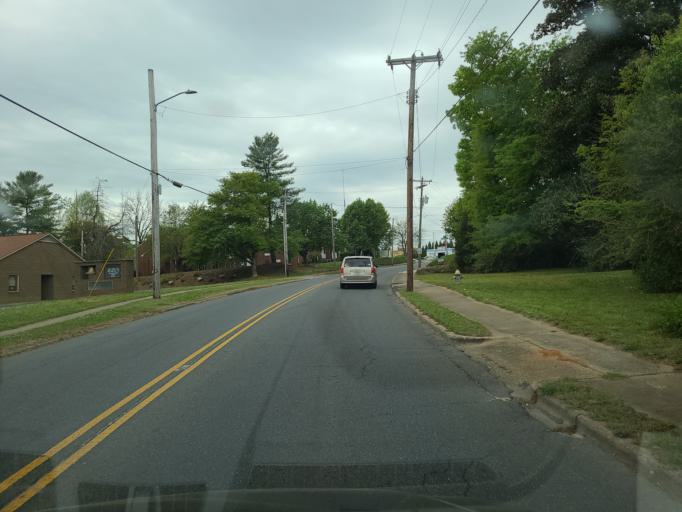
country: US
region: North Carolina
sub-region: Cleveland County
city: Shelby
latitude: 35.2919
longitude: -81.5326
